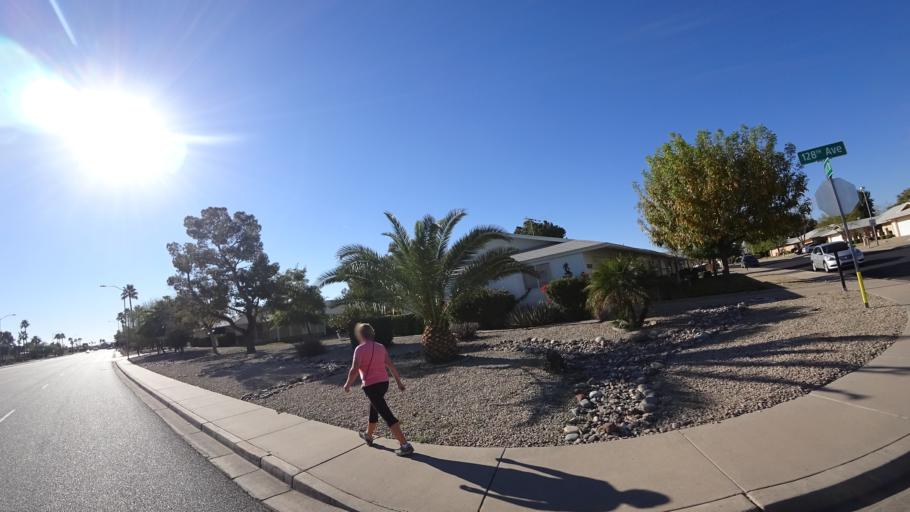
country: US
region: Arizona
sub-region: Maricopa County
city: Sun City West
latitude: 33.6520
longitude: -112.3348
